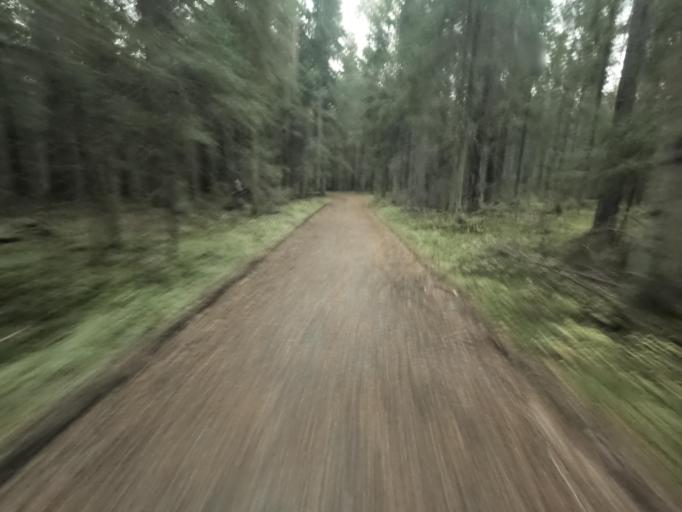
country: RU
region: Leningrad
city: Leninskoye
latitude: 60.1991
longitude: 29.8410
